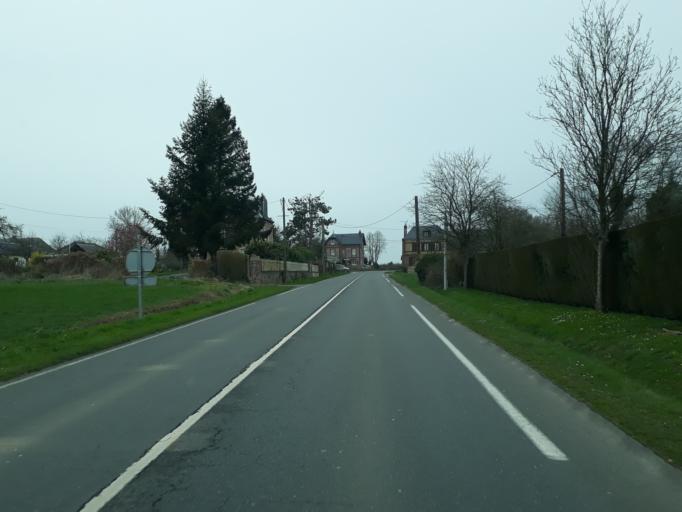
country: FR
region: Haute-Normandie
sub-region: Departement de la Seine-Maritime
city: Beuzeville-la-Grenier
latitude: 49.5951
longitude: 0.4226
